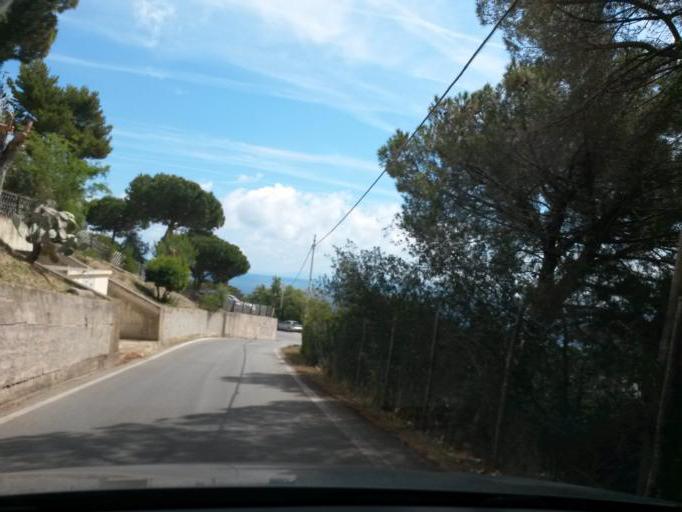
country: IT
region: Tuscany
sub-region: Provincia di Livorno
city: Porto Azzurro
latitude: 42.7554
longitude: 10.3953
